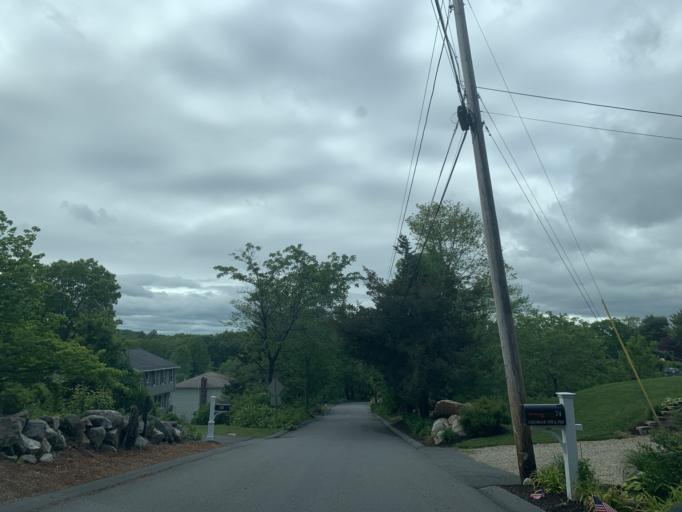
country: US
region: Massachusetts
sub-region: Worcester County
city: Grafton
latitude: 42.2012
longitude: -71.6495
